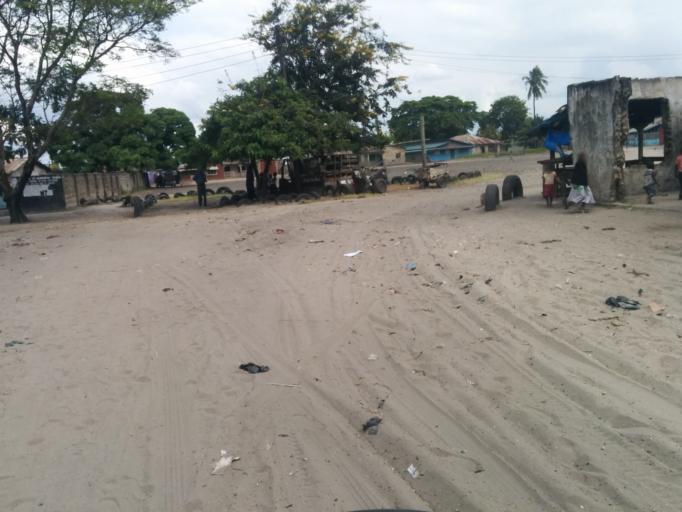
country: TZ
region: Dar es Salaam
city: Dar es Salaam
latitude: -6.8653
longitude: 39.2539
